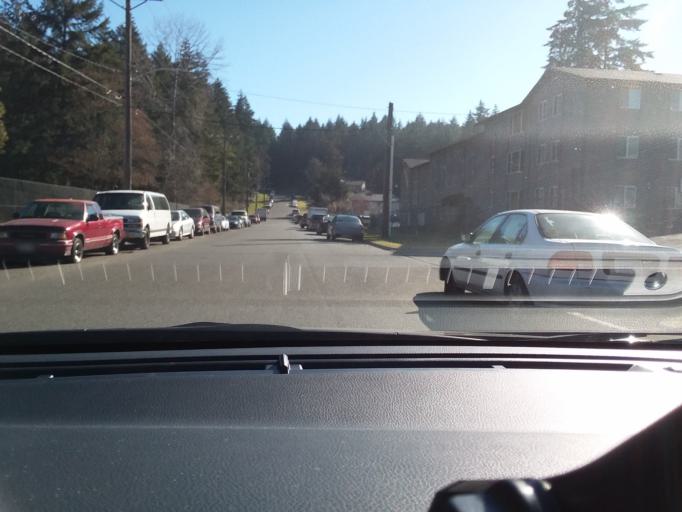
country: US
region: Washington
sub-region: Pierce County
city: Waller
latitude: 47.2062
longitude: -122.4038
